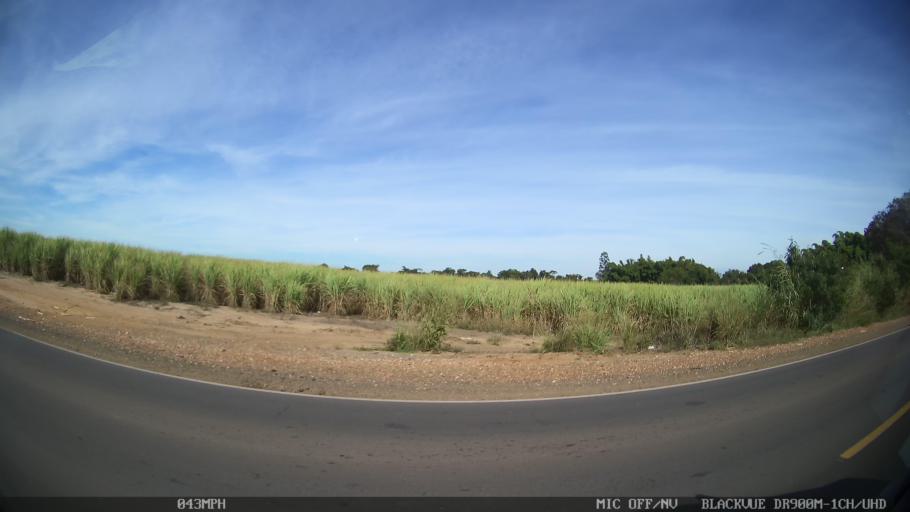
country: BR
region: Sao Paulo
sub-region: Rio Das Pedras
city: Rio das Pedras
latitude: -22.7902
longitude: -47.6294
